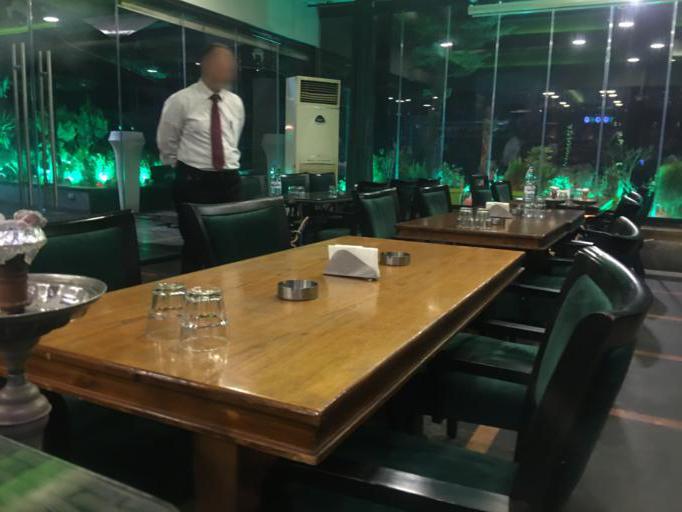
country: SY
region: Rif-dimashq
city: Darayya
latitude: 33.4906
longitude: 36.2444
